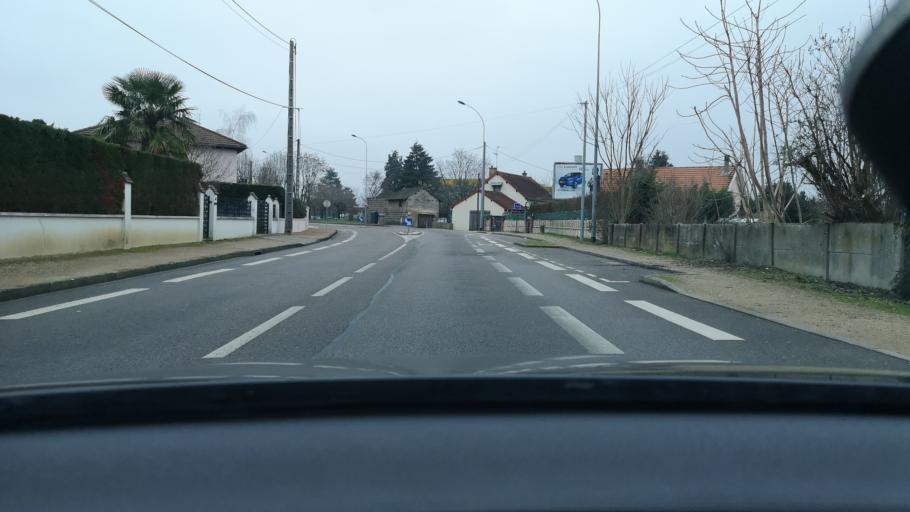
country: FR
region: Bourgogne
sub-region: Departement de Saone-et-Loire
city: Chalon-sur-Saone
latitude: 46.8035
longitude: 4.8533
